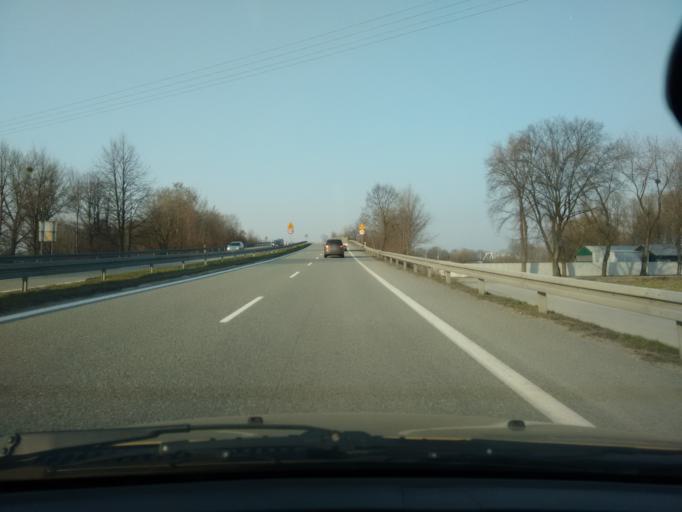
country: PL
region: Silesian Voivodeship
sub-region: Powiat cieszynski
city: Drogomysl
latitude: 49.8831
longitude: 18.7456
